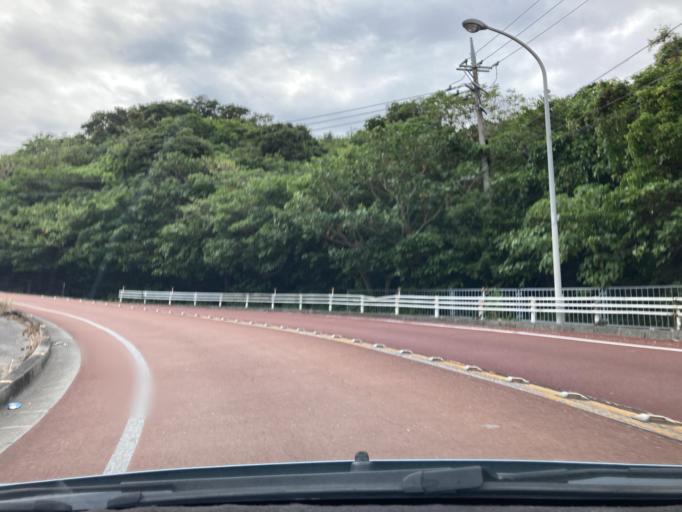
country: JP
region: Okinawa
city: Tomigusuku
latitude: 26.1670
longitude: 127.7709
